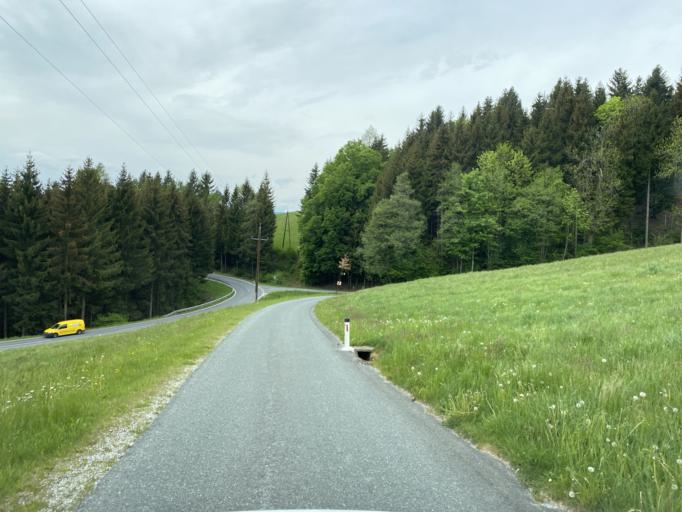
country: AT
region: Styria
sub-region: Politischer Bezirk Weiz
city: Gschaid bei Birkfeld
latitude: 47.3454
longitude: 15.7409
